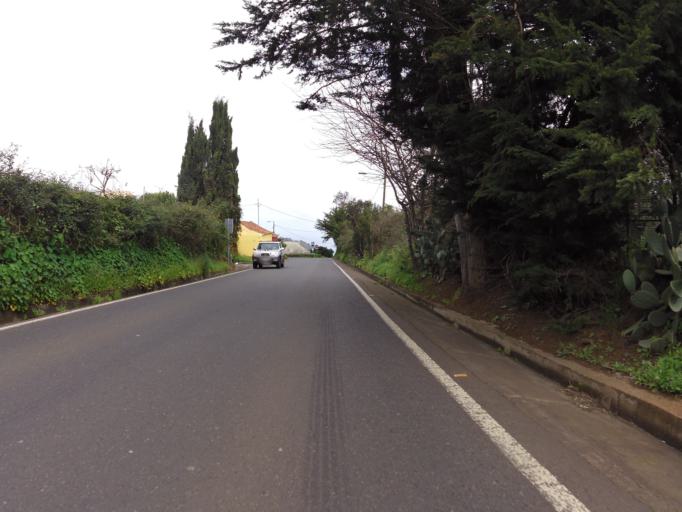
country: ES
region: Canary Islands
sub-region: Provincia de Las Palmas
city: Teror
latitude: 28.0895
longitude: -15.5361
